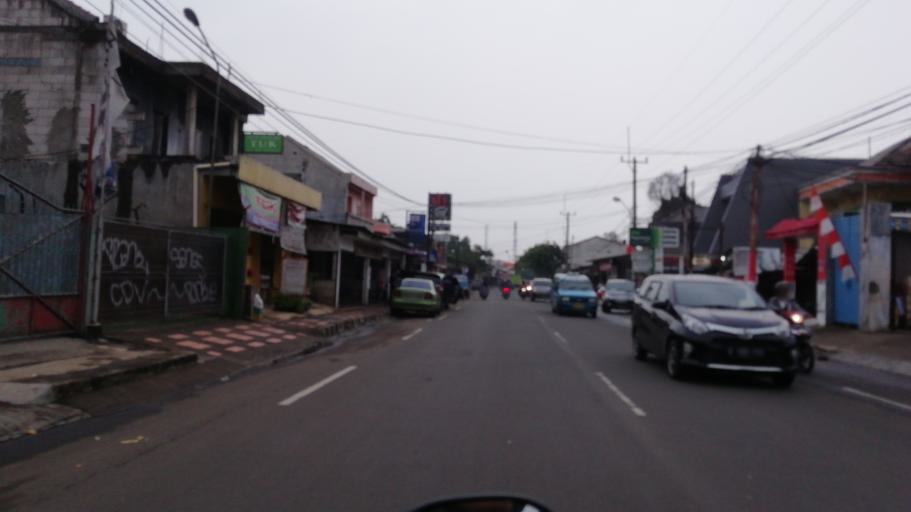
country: ID
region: West Java
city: Cibinong
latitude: -6.4974
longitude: 106.8110
